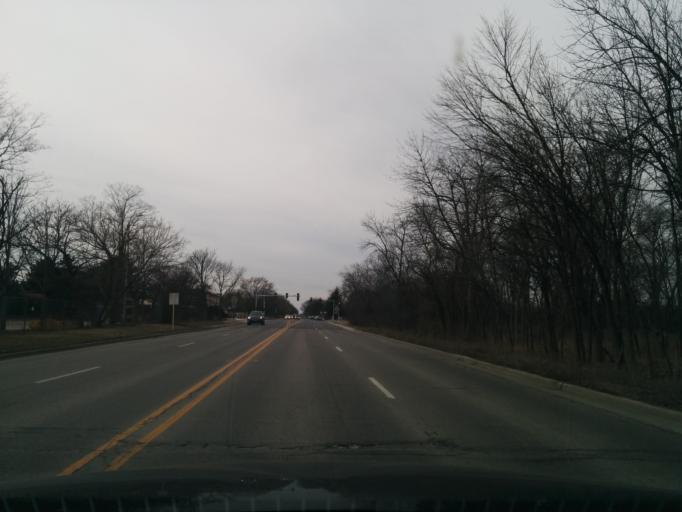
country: US
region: Illinois
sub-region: Cook County
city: Riverside
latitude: 41.8354
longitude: -87.8312
